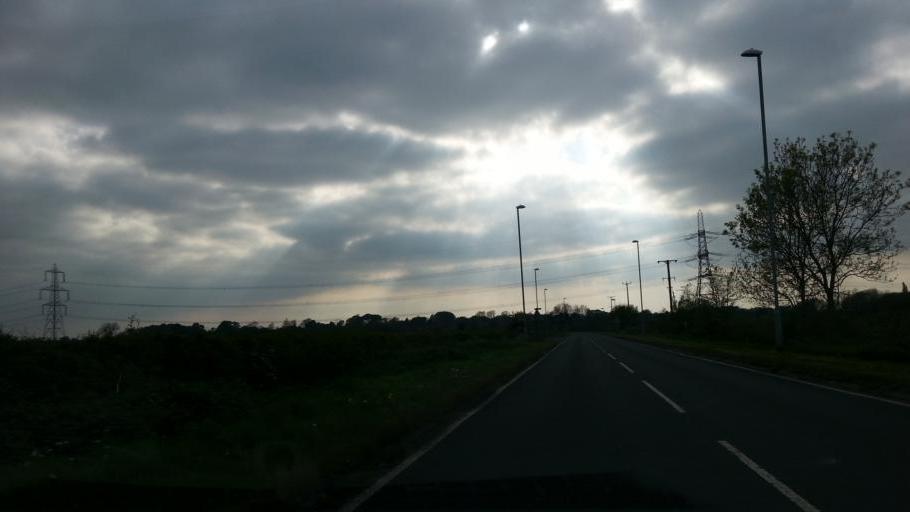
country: GB
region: England
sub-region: Nottinghamshire
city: South Collingham
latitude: 53.0822
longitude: -0.7415
